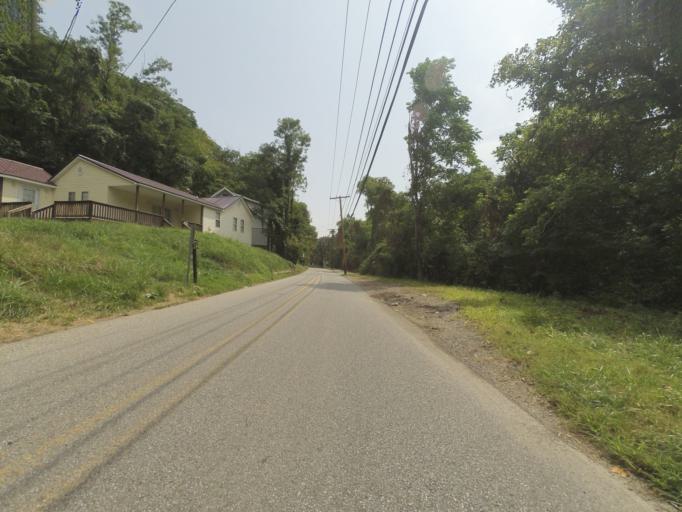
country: US
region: West Virginia
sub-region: Cabell County
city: Huntington
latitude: 38.3985
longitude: -82.4701
